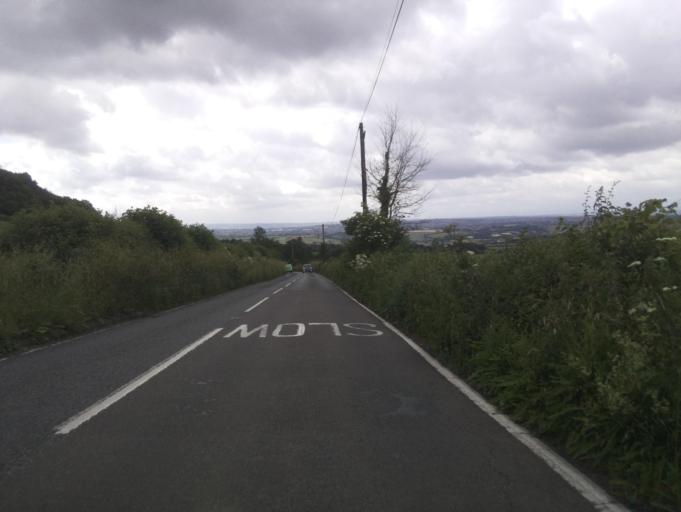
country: GB
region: England
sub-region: South Gloucestershire
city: Cold Ashton
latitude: 51.4334
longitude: -2.4008
